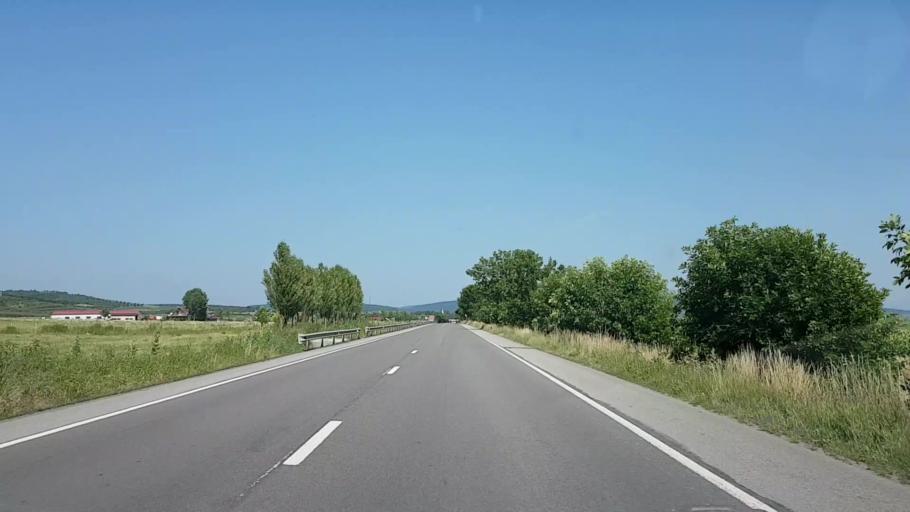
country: RO
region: Bistrita-Nasaud
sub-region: Comuna Petru Rares
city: Reteag
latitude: 47.1982
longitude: 24.0319
